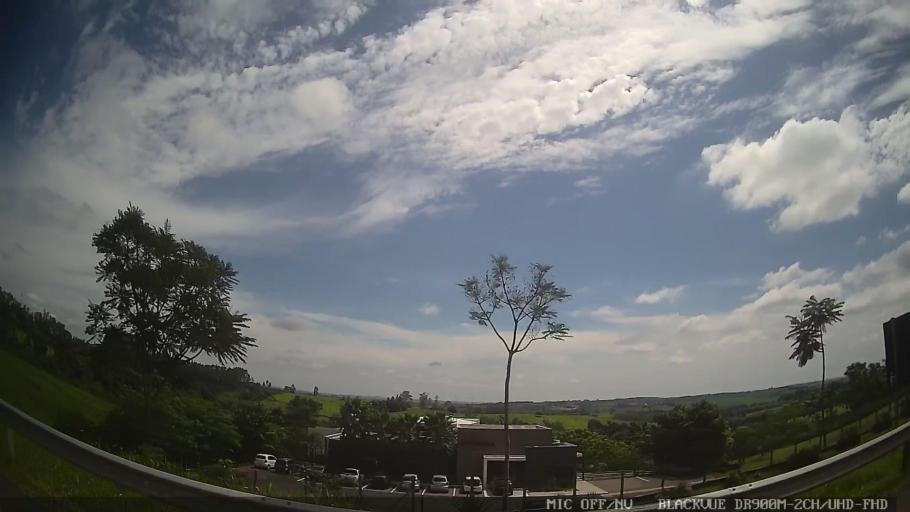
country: BR
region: Sao Paulo
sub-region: Laranjal Paulista
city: Laranjal Paulista
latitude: -23.0837
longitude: -47.7876
